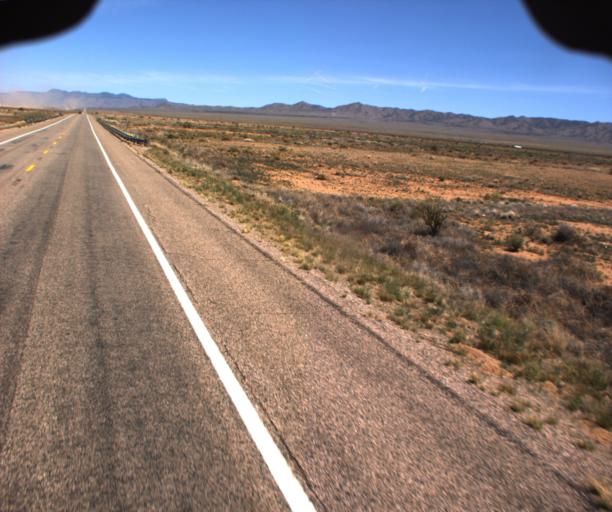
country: US
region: Arizona
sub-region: Mohave County
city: New Kingman-Butler
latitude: 35.3185
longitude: -113.9138
